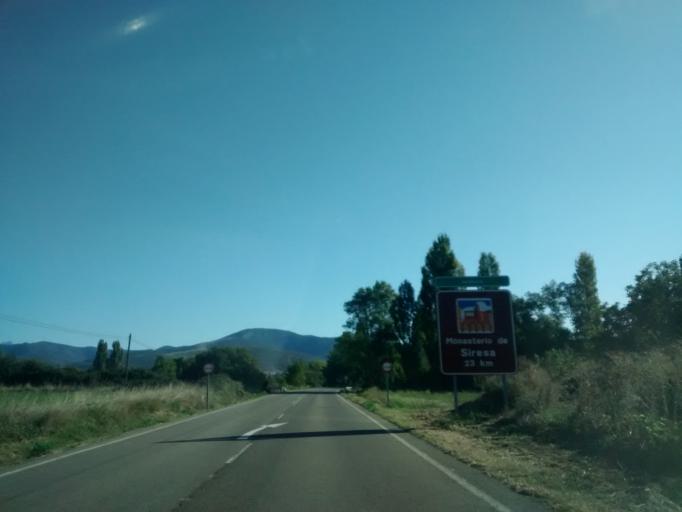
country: ES
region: Aragon
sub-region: Provincia de Huesca
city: Bailo
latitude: 42.5750
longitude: -0.7603
